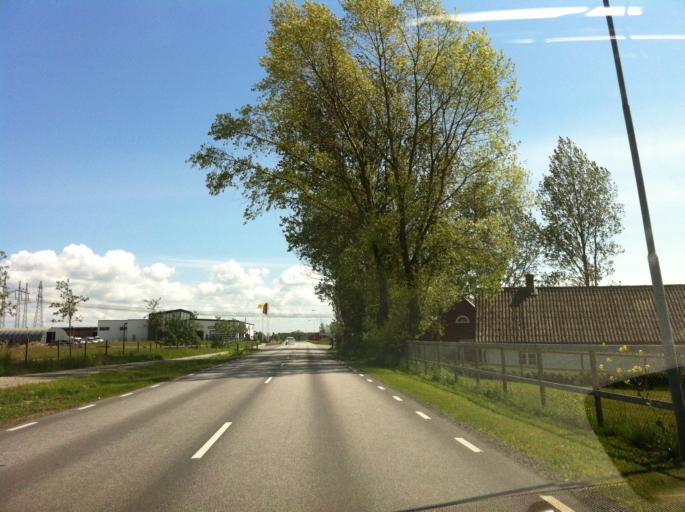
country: SE
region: Skane
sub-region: Kavlinge Kommun
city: Loddekopinge
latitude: 55.7898
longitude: 13.0000
